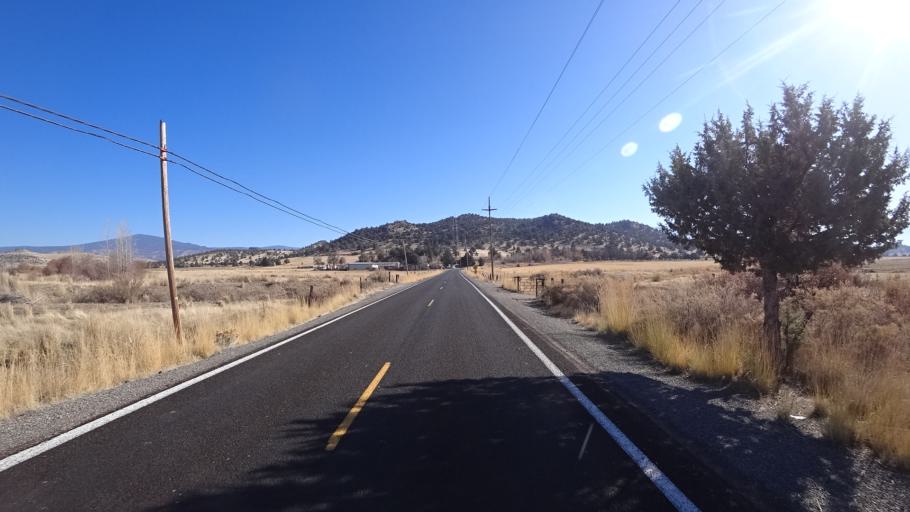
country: US
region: California
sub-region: Siskiyou County
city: Montague
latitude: 41.7114
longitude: -122.3836
